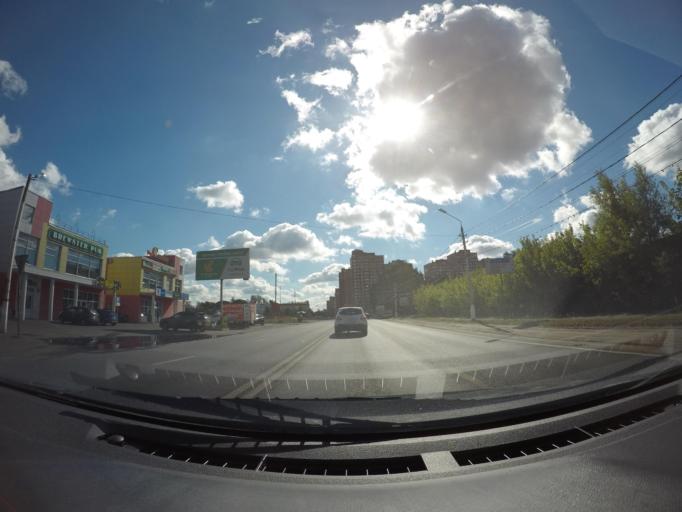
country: RU
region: Moskovskaya
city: Ramenskoye
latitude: 55.5831
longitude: 38.2414
